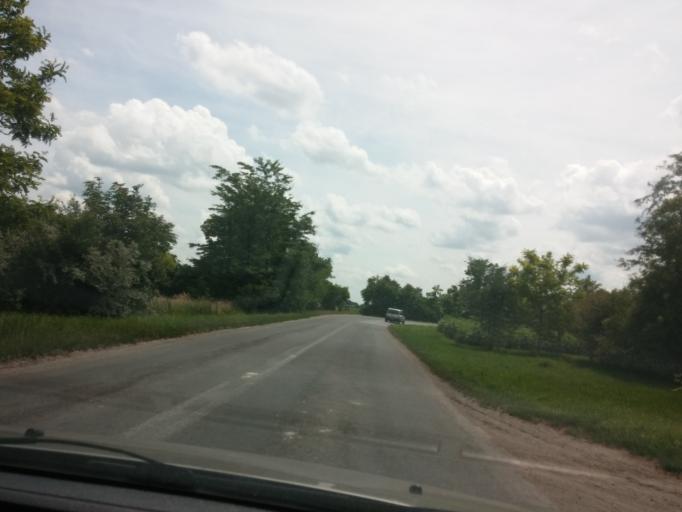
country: HU
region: Pest
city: Szigetcsep
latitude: 47.2863
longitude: 18.9833
